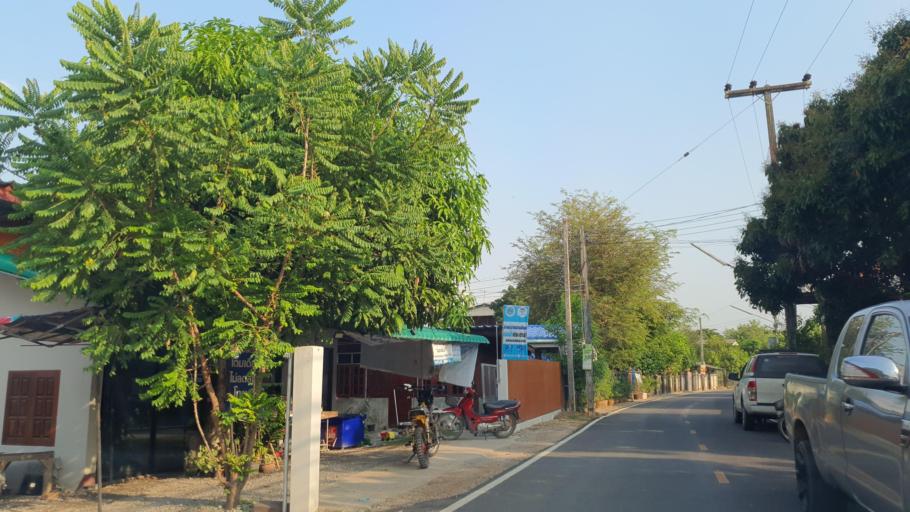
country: TH
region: Chiang Mai
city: Mae Wang
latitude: 18.6122
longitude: 98.8215
